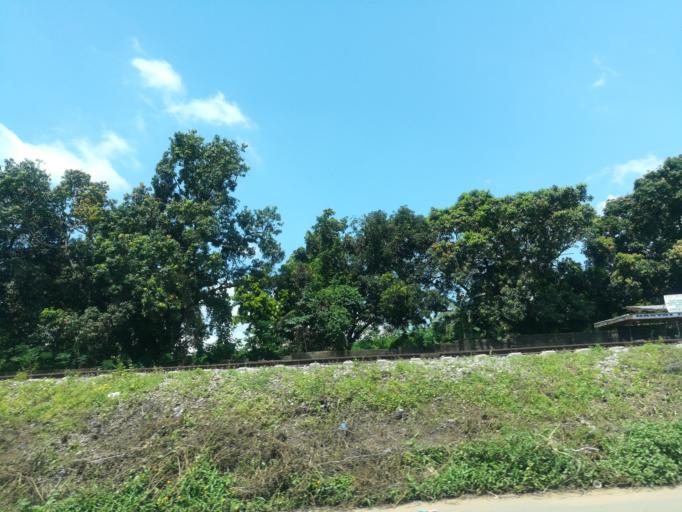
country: NG
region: Oyo
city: Ibadan
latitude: 7.3815
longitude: 3.8679
